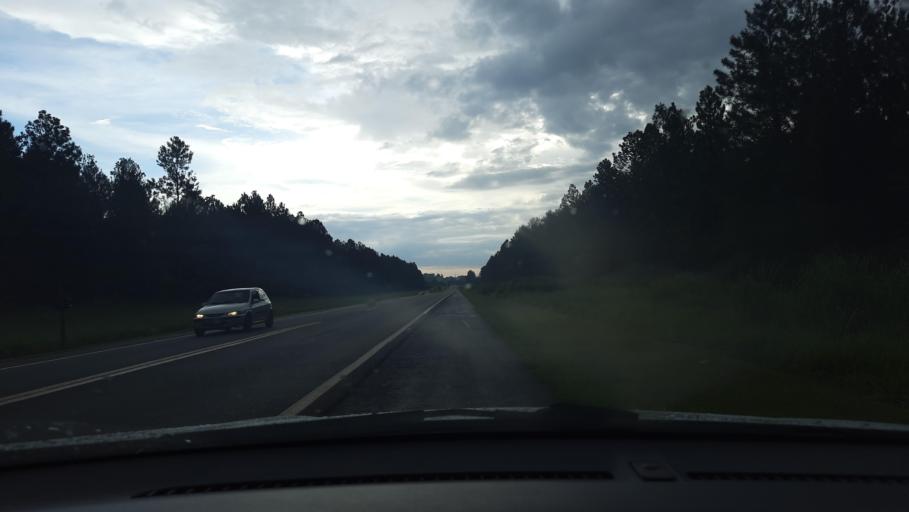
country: BR
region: Sao Paulo
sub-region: Casa Branca
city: Casa Branca
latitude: -21.7696
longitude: -47.0469
